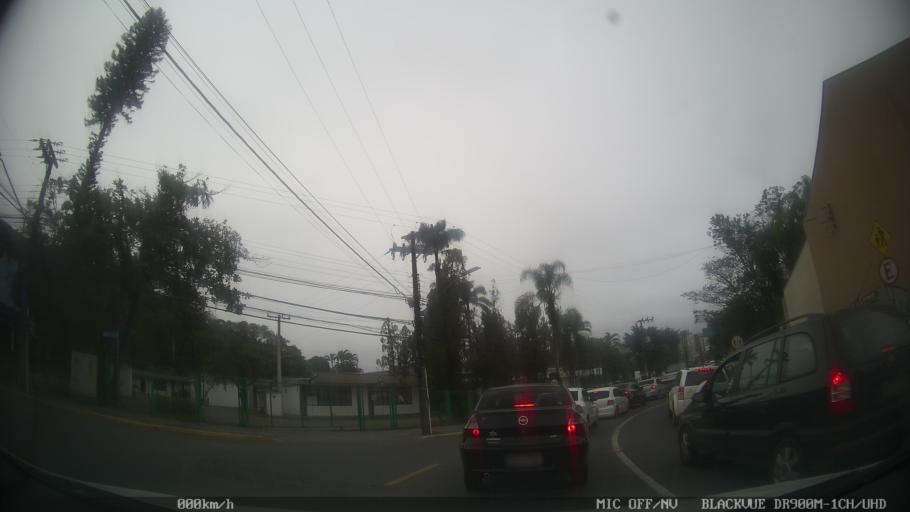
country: BR
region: Santa Catarina
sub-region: Joinville
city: Joinville
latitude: -26.2950
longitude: -48.8412
